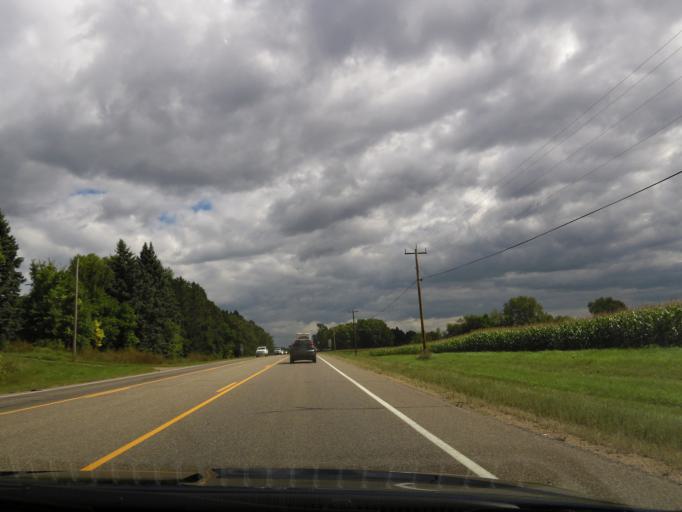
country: US
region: Minnesota
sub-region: Dakota County
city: Rosemount
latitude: 44.7174
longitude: -93.0954
